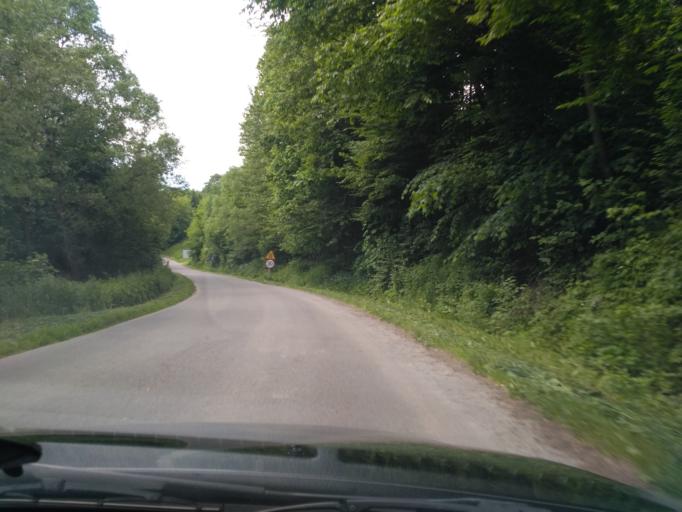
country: PL
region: Subcarpathian Voivodeship
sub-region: Powiat brzozowski
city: Wesola
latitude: 49.8065
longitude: 22.0806
